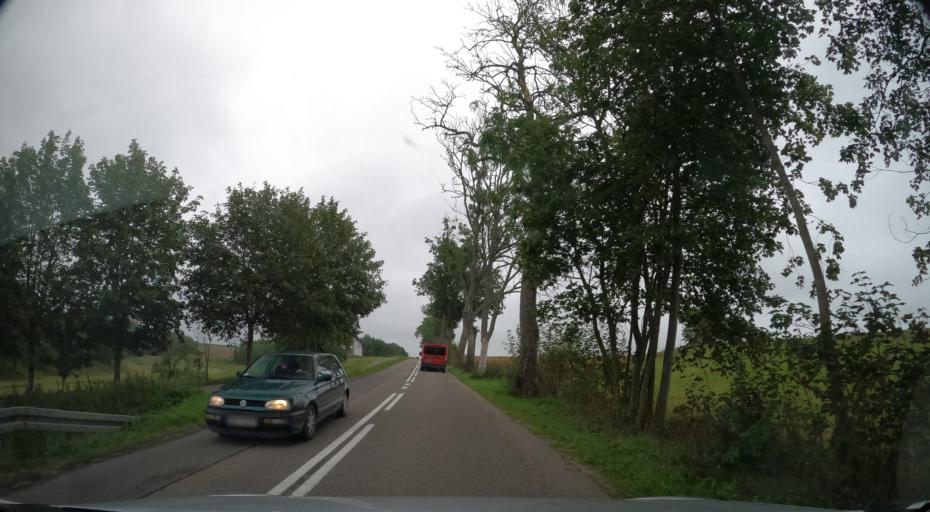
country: PL
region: Pomeranian Voivodeship
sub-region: Powiat wejherowski
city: Luzino
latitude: 54.4938
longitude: 18.1378
